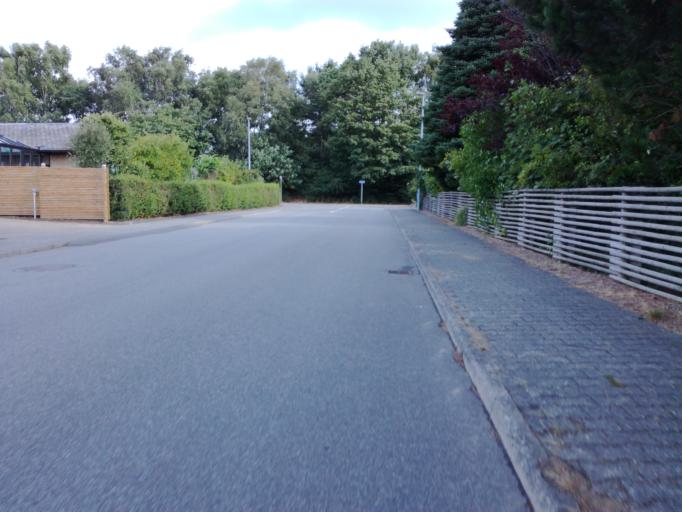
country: DK
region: South Denmark
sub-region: Fredericia Kommune
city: Fredericia
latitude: 55.5824
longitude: 9.7857
